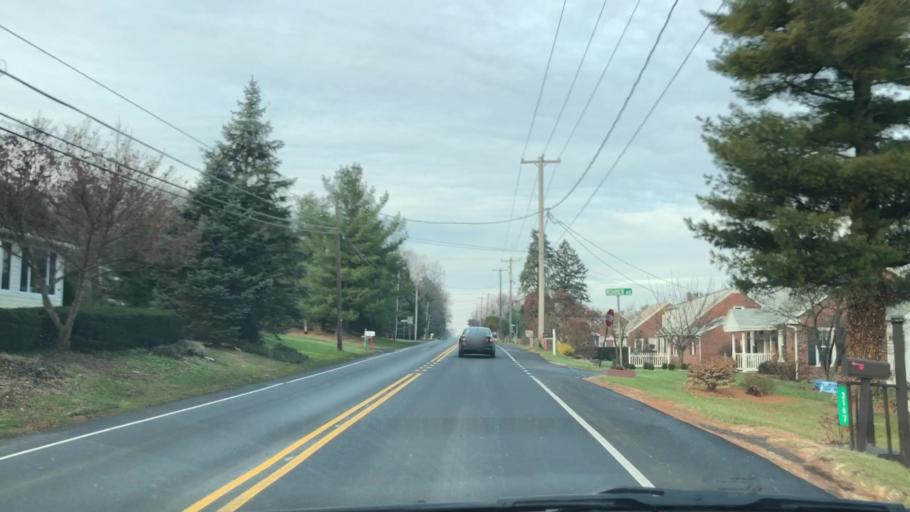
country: US
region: Pennsylvania
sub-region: Lancaster County
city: Mountville
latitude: 40.0590
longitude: -76.4063
